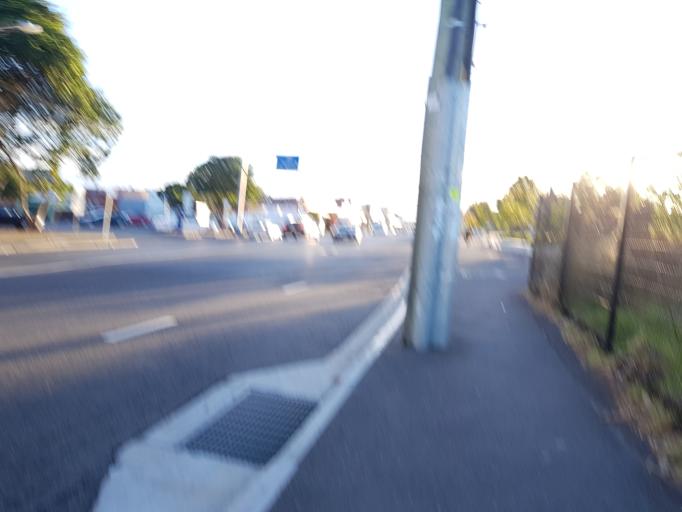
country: AU
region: Victoria
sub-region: Maribyrnong
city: Footscray
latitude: -37.8022
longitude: 144.8995
